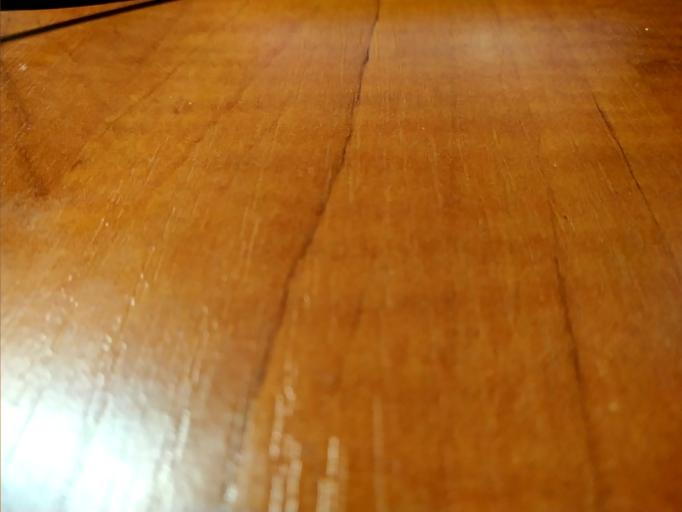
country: RU
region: Tverskaya
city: Spirovo
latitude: 57.3728
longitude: 34.9742
